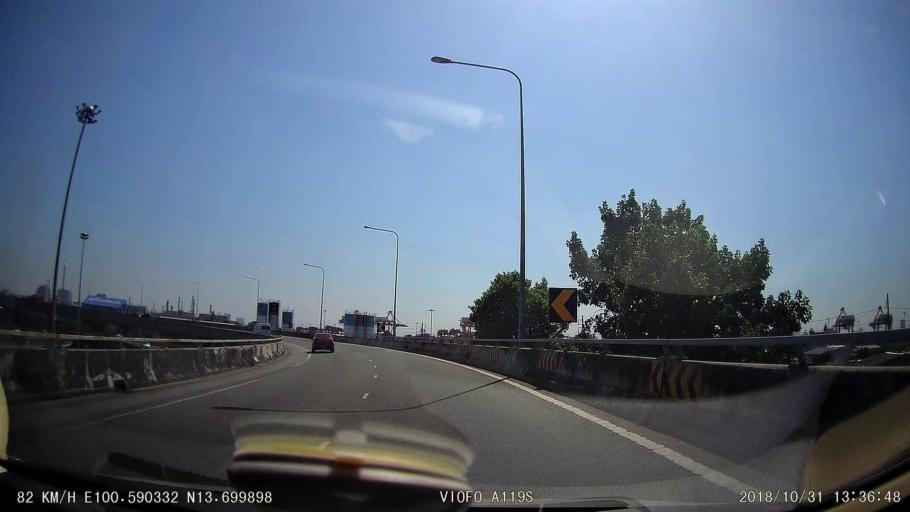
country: TH
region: Bangkok
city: Phra Khanong
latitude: 13.6997
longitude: 100.5897
